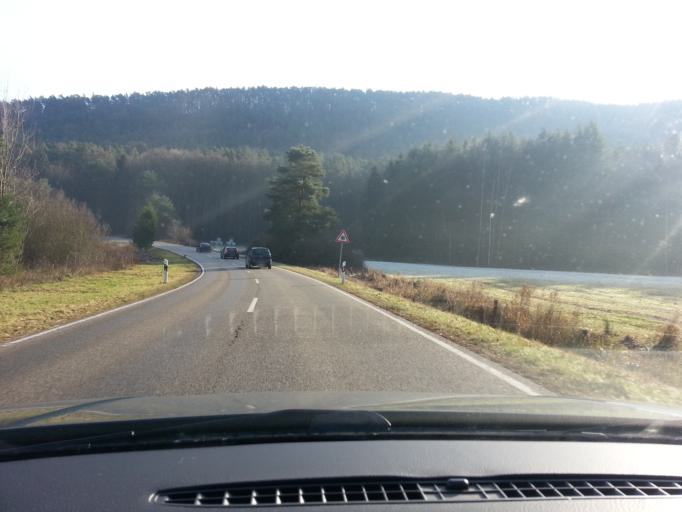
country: DE
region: Rheinland-Pfalz
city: Hauenstein
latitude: 49.1841
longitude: 7.8641
